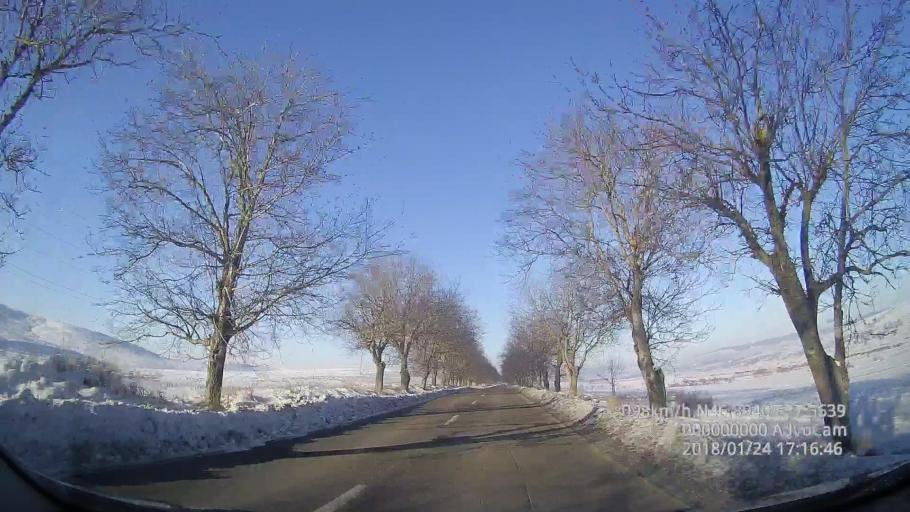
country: RO
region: Iasi
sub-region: Comuna Scanteia
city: Scanteia
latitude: 46.8947
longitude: 27.5639
